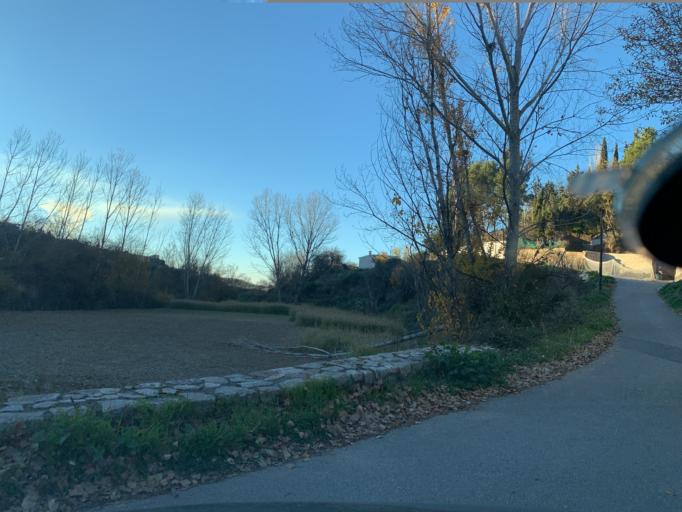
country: ES
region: Andalusia
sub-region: Provincia de Granada
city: Dilar
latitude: 37.0691
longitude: -3.5804
